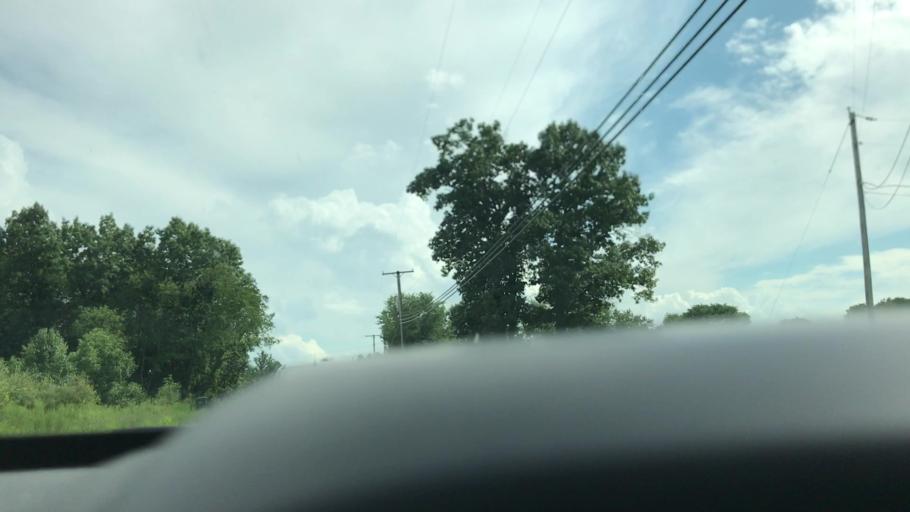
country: US
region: Ohio
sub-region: Stark County
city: Brewster
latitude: 40.7520
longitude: -81.5952
